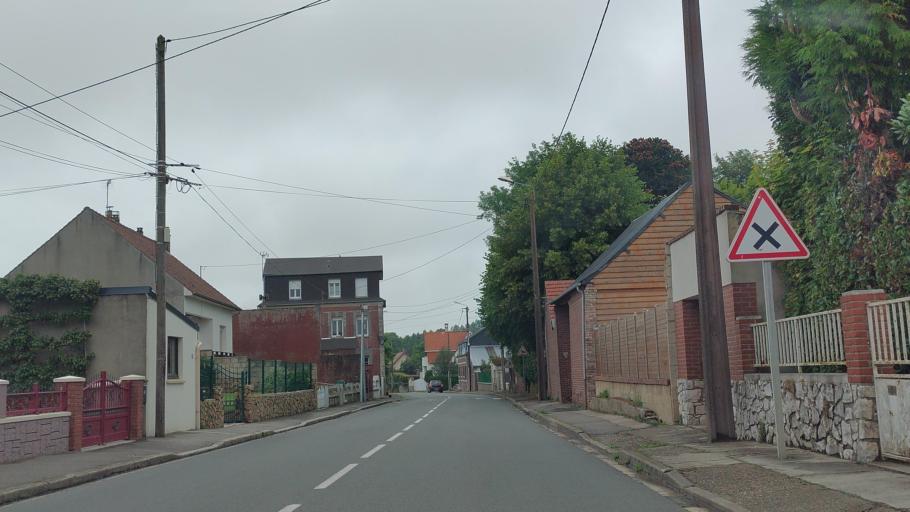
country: FR
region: Picardie
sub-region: Departement de la Somme
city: Bethencourt-sur-Mer
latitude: 50.0858
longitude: 1.4921
